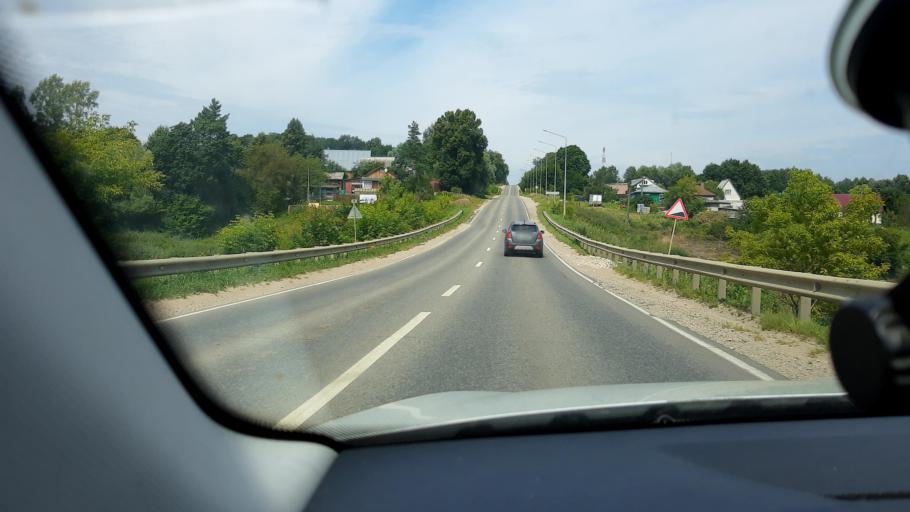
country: RU
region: Tula
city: Zaokskiy
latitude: 54.7551
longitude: 37.4381
